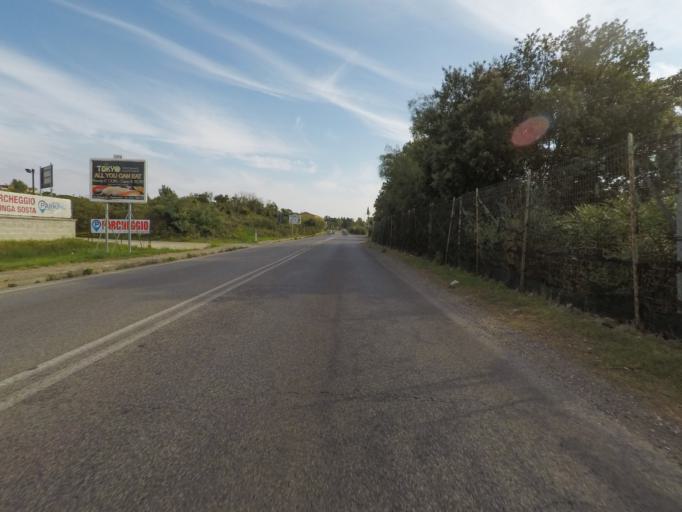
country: IT
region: Latium
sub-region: Citta metropolitana di Roma Capitale
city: Civitavecchia
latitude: 42.0629
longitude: 11.8150
